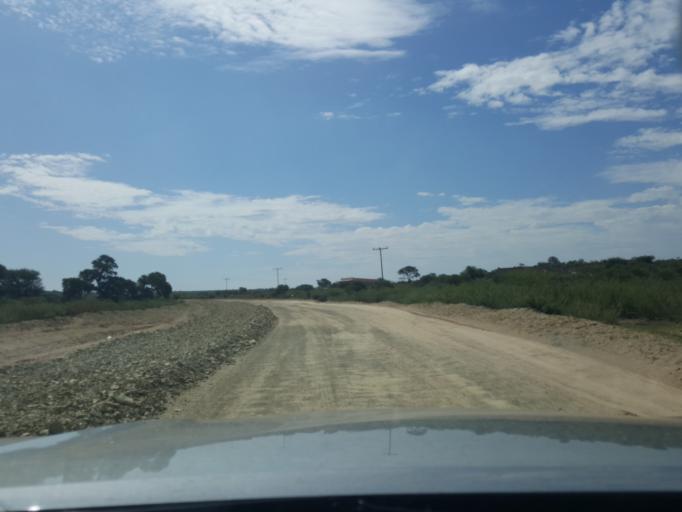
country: BW
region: Kweneng
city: Letlhakeng
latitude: -23.9880
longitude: 24.9714
